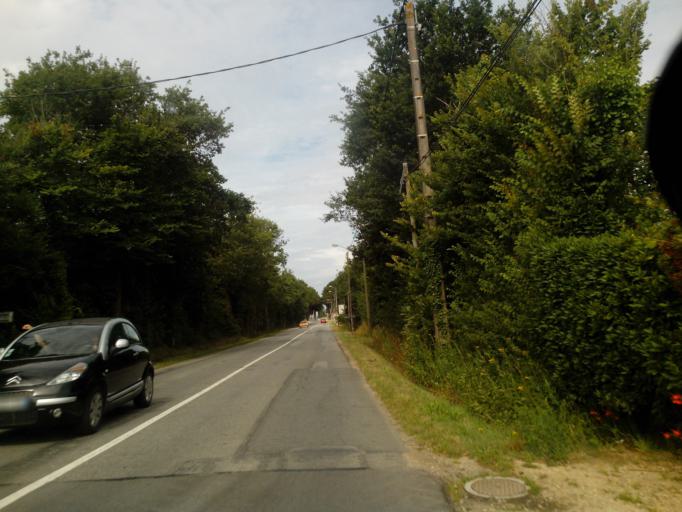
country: FR
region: Brittany
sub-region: Departement du Morbihan
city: Ploemel
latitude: 47.6664
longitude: -3.0367
